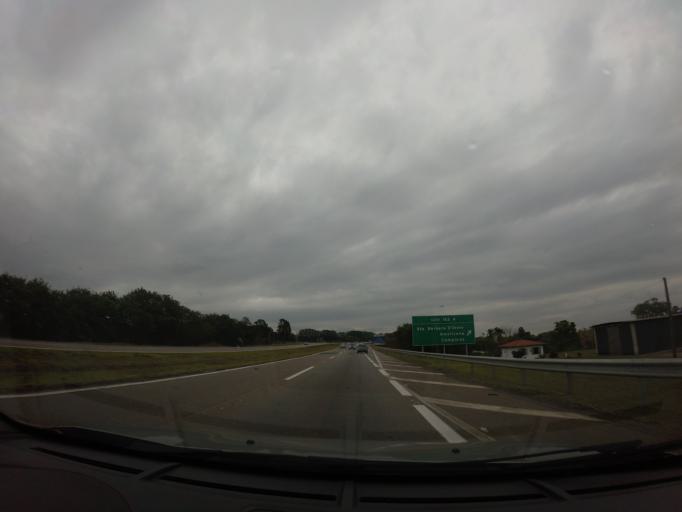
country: BR
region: Sao Paulo
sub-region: Piracicaba
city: Piracicaba
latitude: -22.7255
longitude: -47.6051
